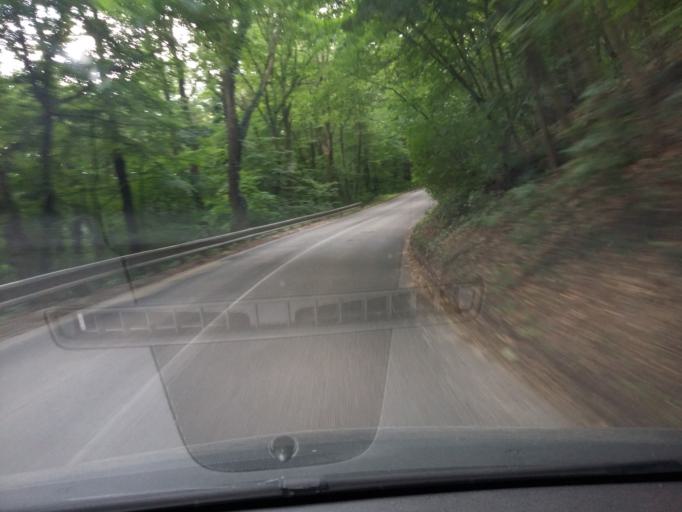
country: SK
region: Trnavsky
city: Smolenice
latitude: 48.5399
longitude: 17.3495
